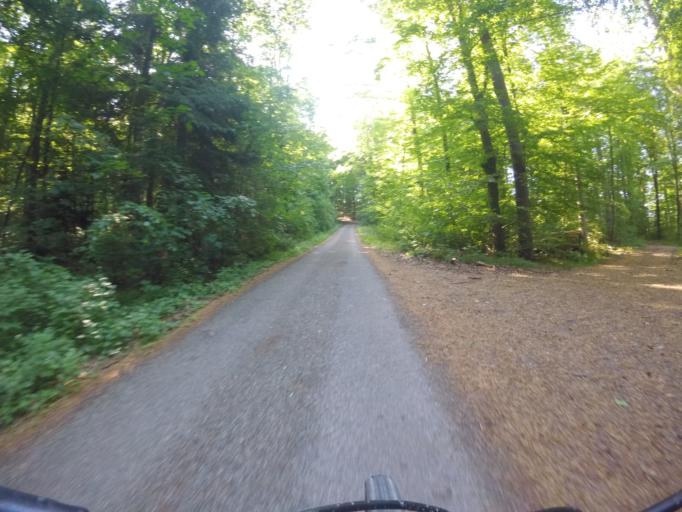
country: DE
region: Baden-Wuerttemberg
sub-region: Regierungsbezirk Stuttgart
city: Aspach
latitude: 48.9843
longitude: 9.4173
